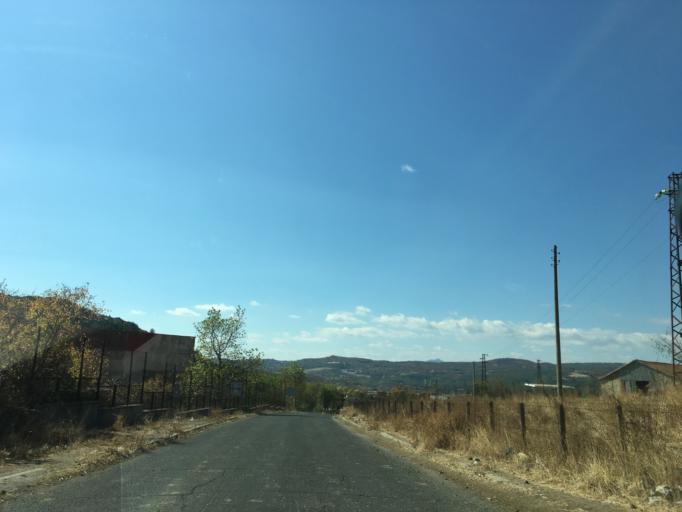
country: BG
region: Kurdzhali
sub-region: Obshtina Dzhebel
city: Dzhebel
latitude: 41.5190
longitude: 25.4232
